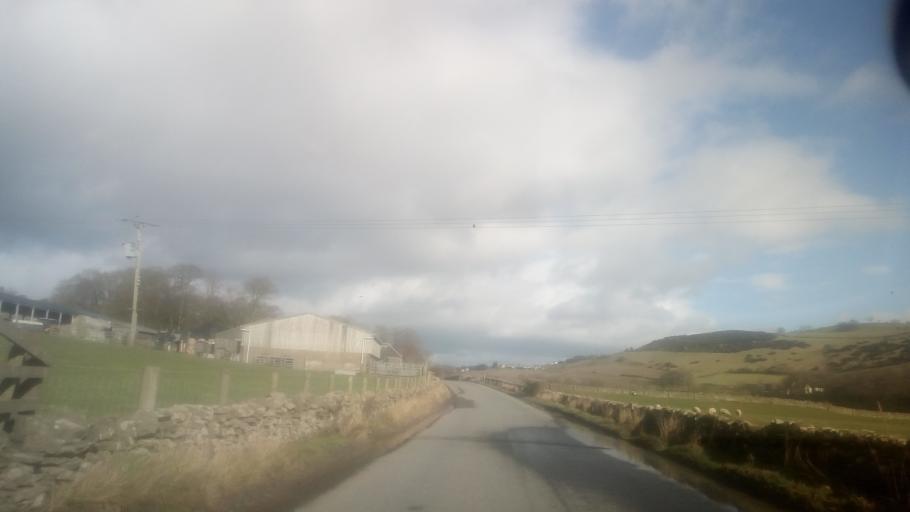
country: GB
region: Scotland
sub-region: The Scottish Borders
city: Hawick
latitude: 55.4116
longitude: -2.8291
